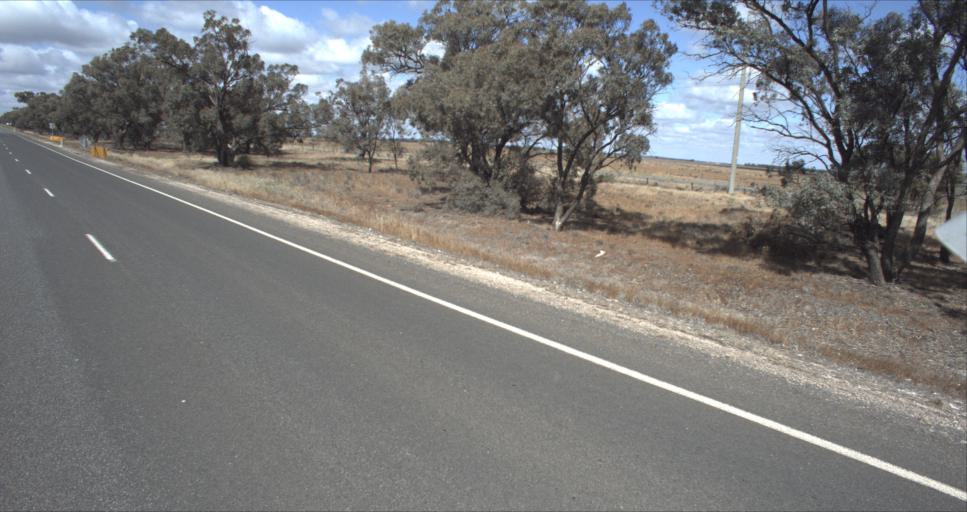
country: AU
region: New South Wales
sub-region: Murrumbidgee Shire
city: Darlington Point
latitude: -34.5549
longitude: 146.1701
